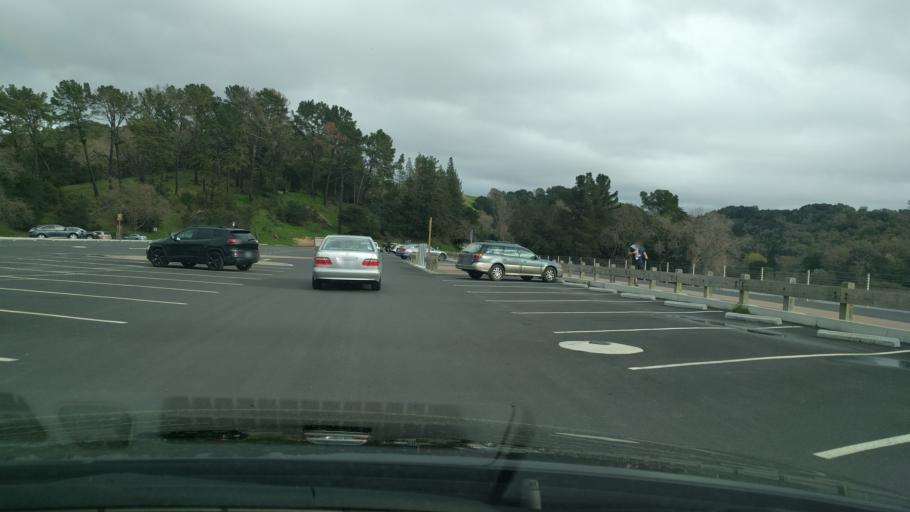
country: US
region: California
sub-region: Contra Costa County
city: Lafayette
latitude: 37.8846
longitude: -122.1389
